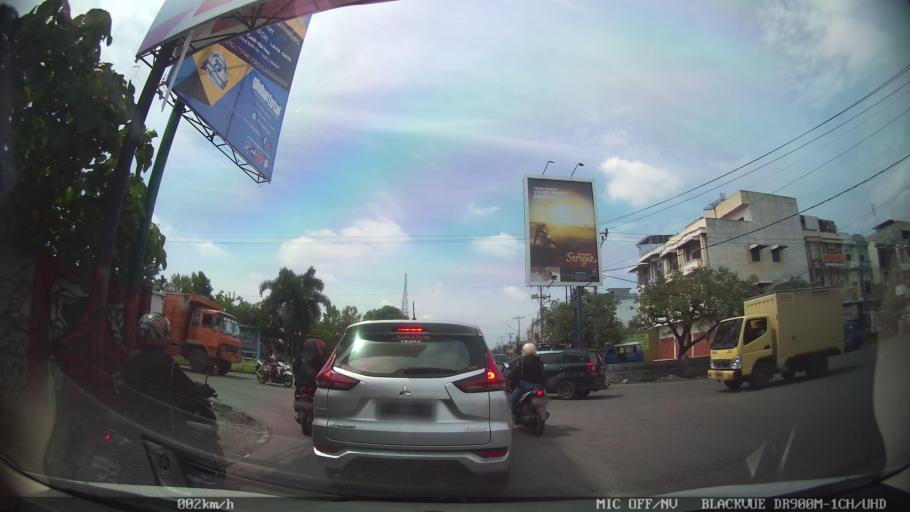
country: ID
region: North Sumatra
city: Medan
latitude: 3.6286
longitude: 98.7078
